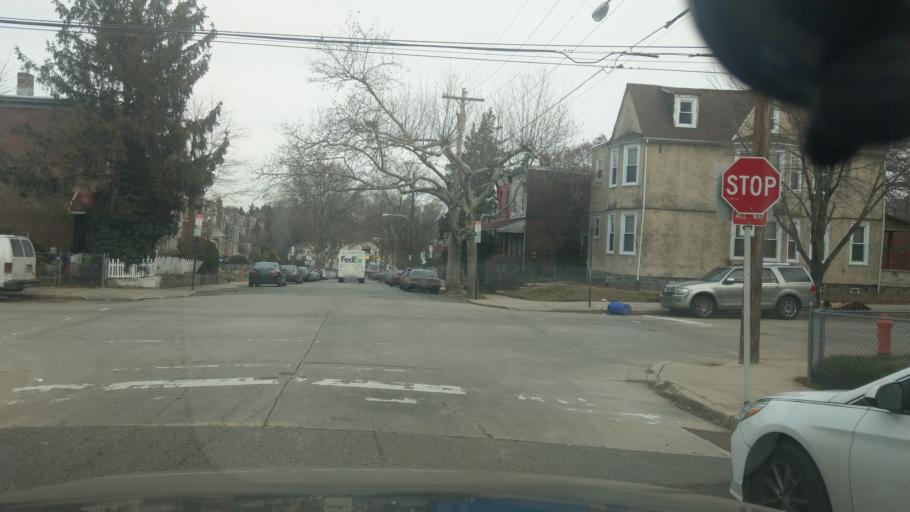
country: US
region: Pennsylvania
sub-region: Montgomery County
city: Wyncote
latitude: 40.0438
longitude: -75.1399
